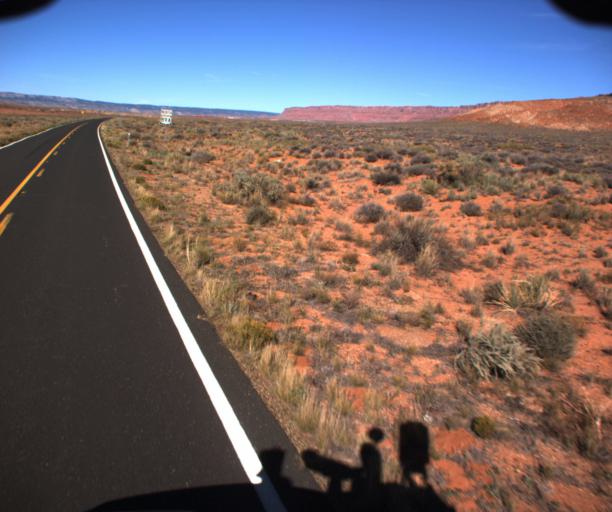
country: US
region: Arizona
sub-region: Coconino County
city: Page
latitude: 36.6840
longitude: -111.8547
